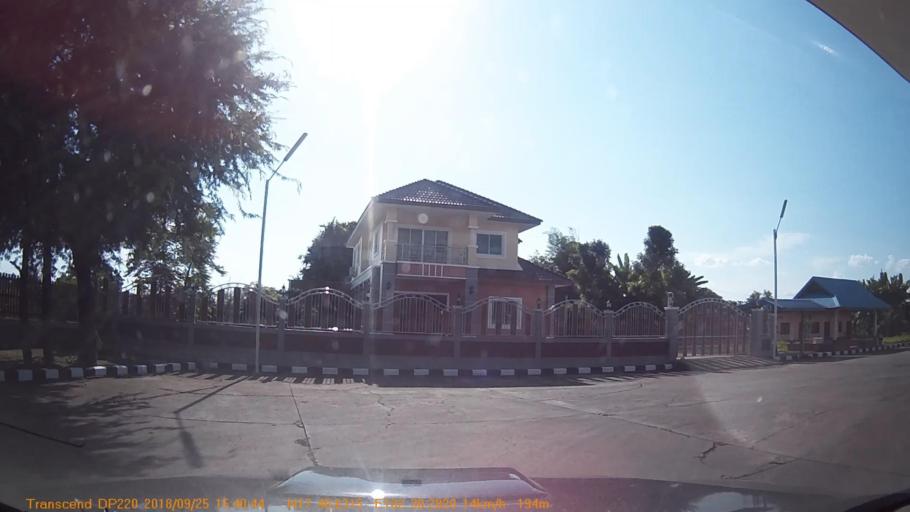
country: TH
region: Changwat Udon Thani
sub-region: Amphoe Ban Phue
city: Ban Phue
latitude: 17.6772
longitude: 102.5046
